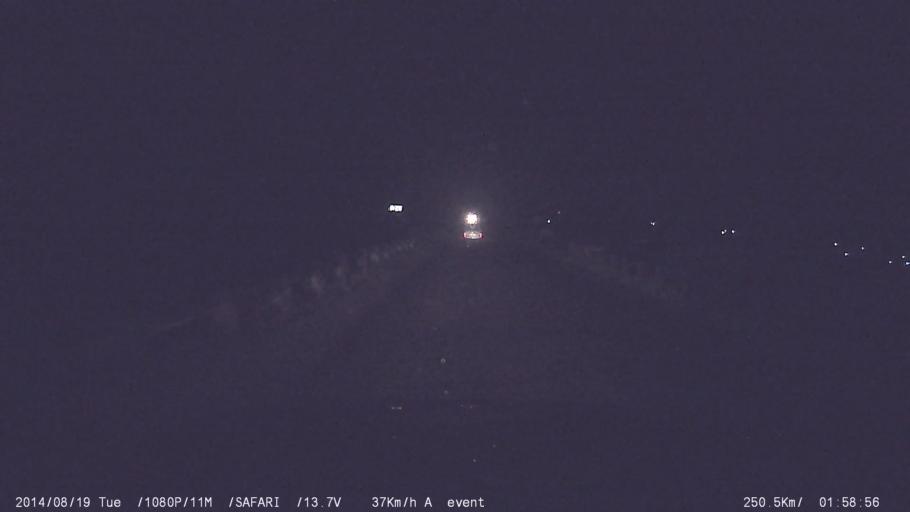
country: IN
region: Tamil Nadu
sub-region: Coimbatore
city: Madukkarai
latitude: 10.8657
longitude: 76.8788
